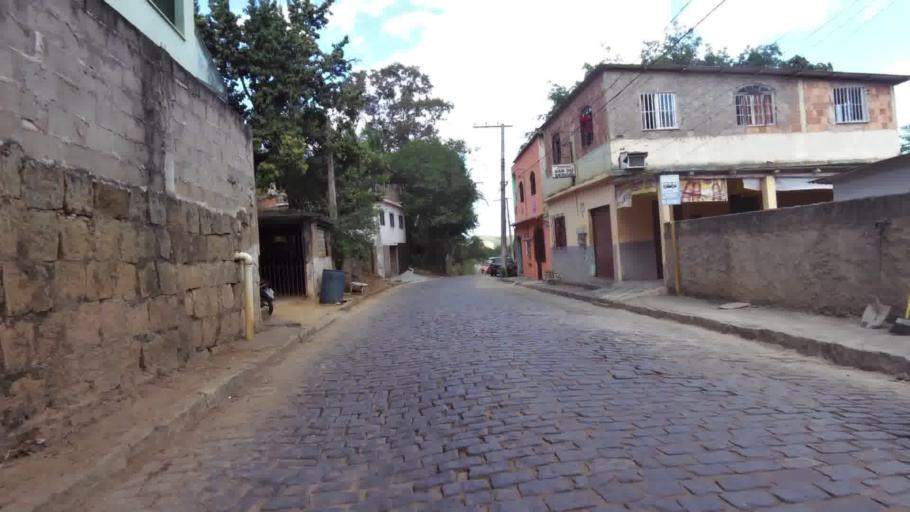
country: BR
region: Espirito Santo
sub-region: Rio Novo Do Sul
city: Rio Novo do Sul
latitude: -20.8694
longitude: -40.9448
